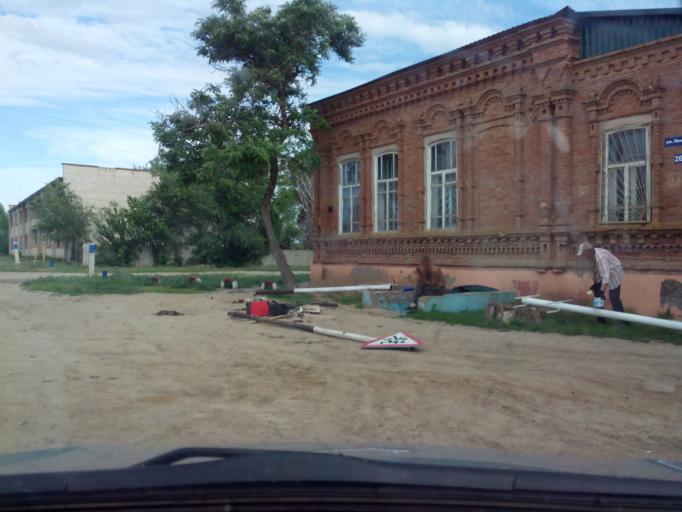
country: RU
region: Volgograd
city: Leninsk
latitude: 48.6674
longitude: 45.3686
